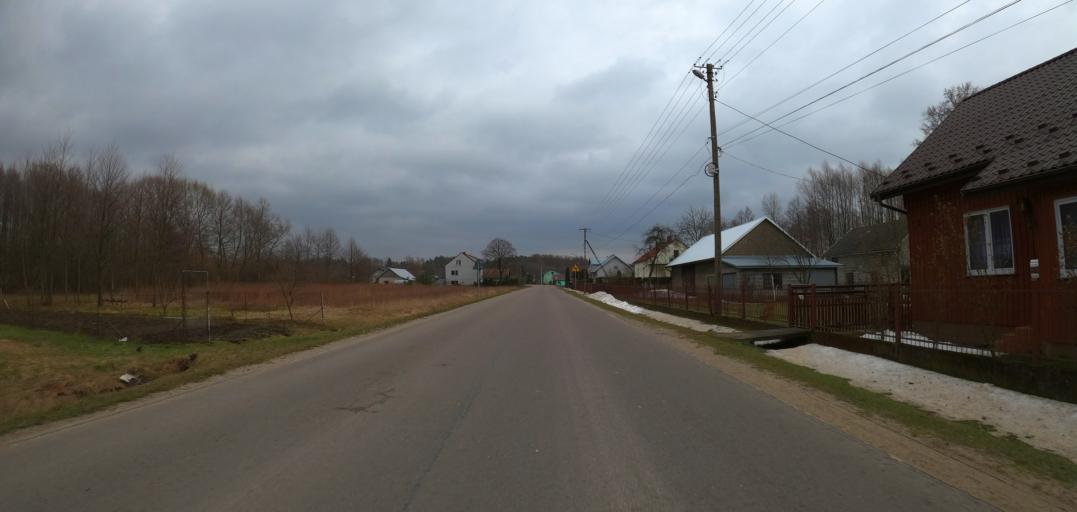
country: PL
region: Subcarpathian Voivodeship
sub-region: Powiat debicki
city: Pilzno
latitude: 49.9795
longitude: 21.3374
